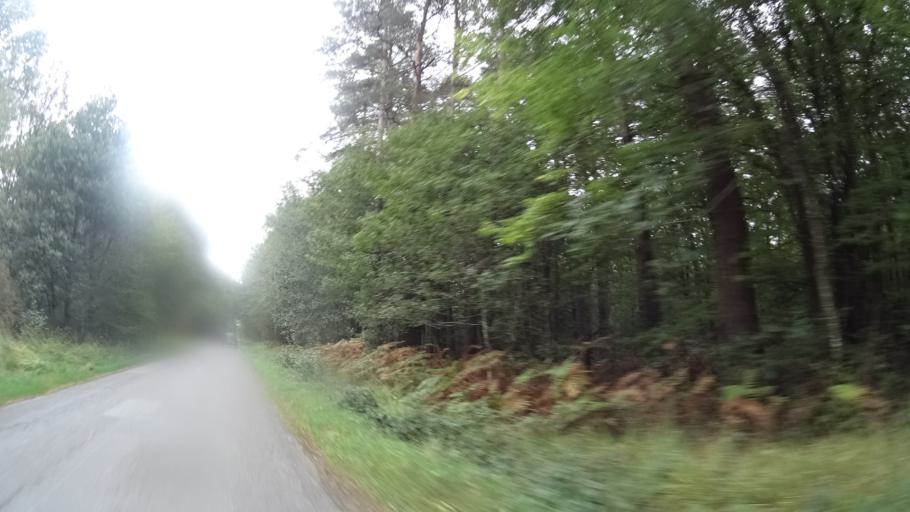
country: FR
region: Brittany
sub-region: Departement d'Ille-et-Vilaine
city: Paimpont
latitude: 48.0788
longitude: -2.1519
